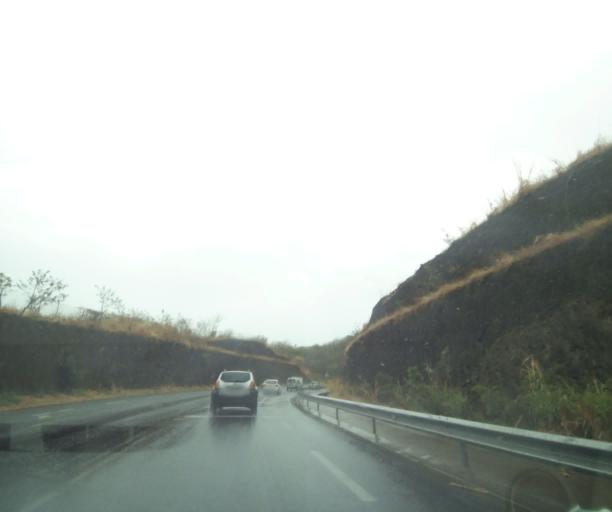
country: RE
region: Reunion
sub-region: Reunion
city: Le Port
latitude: -20.9706
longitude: 55.3121
